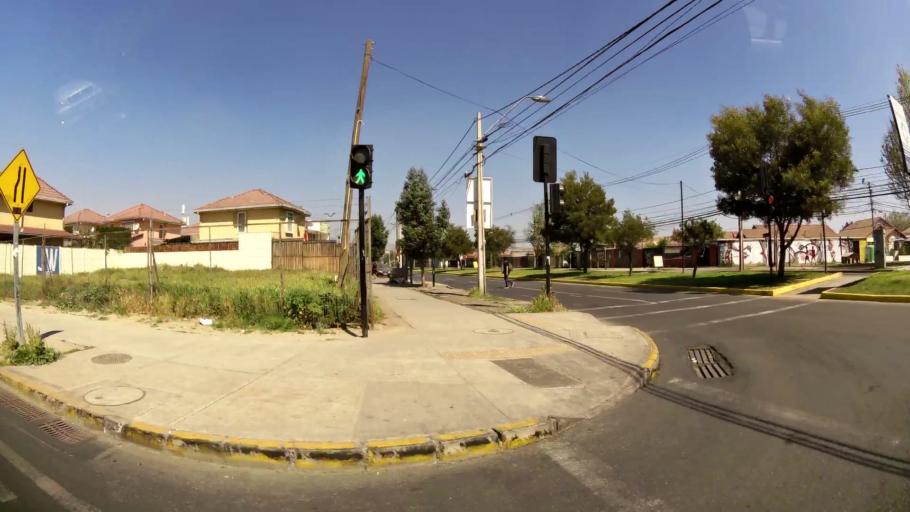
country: CL
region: Santiago Metropolitan
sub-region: Provincia de Santiago
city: Lo Prado
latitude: -33.3529
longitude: -70.7290
